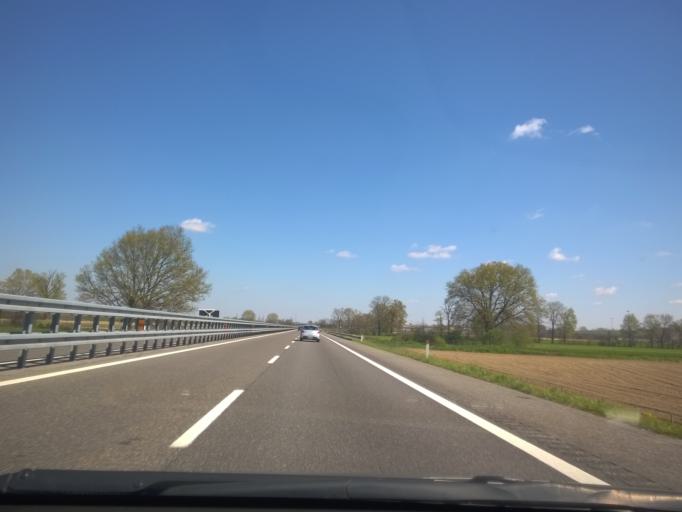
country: IT
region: Lombardy
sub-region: Provincia di Pavia
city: Arena Po
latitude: 45.0842
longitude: 9.3488
